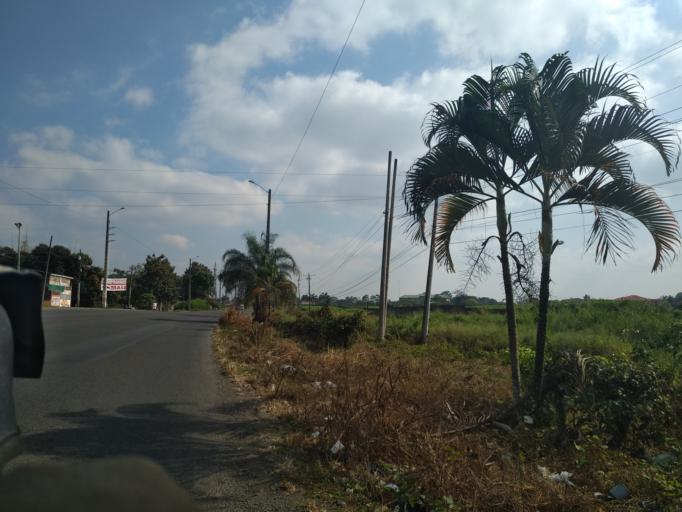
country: EC
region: Los Rios
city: Quevedo
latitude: -1.0662
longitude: -79.4931
